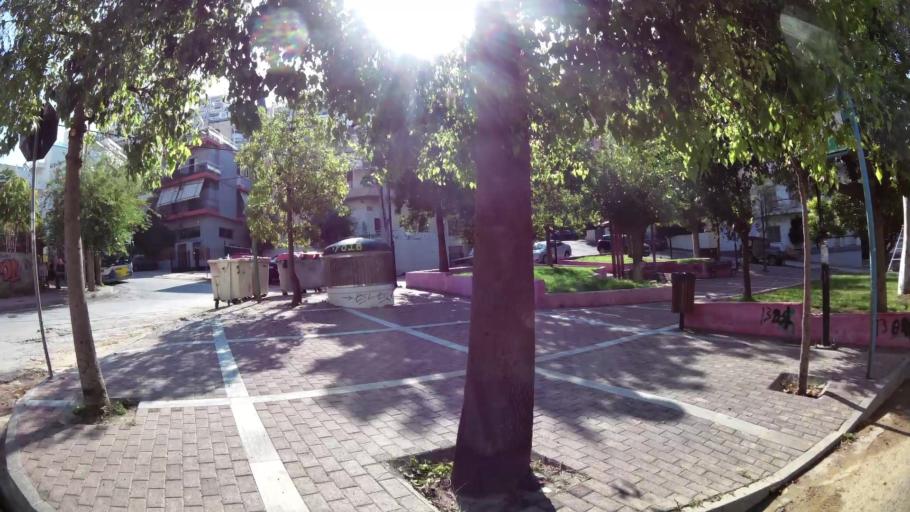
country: GR
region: Attica
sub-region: Nomarchia Athinas
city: Ilioupoli
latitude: 37.9430
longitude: 23.7684
